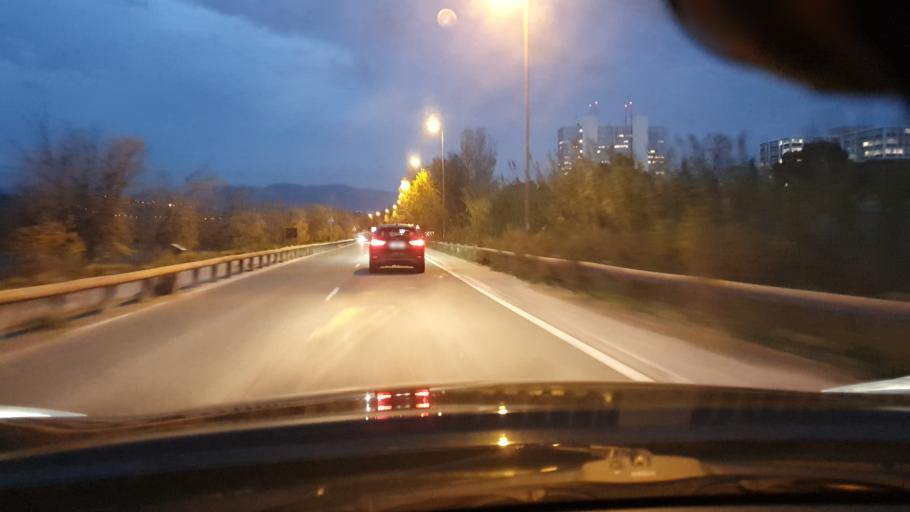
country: FR
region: Provence-Alpes-Cote d'Azur
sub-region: Departement des Alpes-Maritimes
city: Saint-Laurent-du-Var
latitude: 43.6693
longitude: 7.1981
